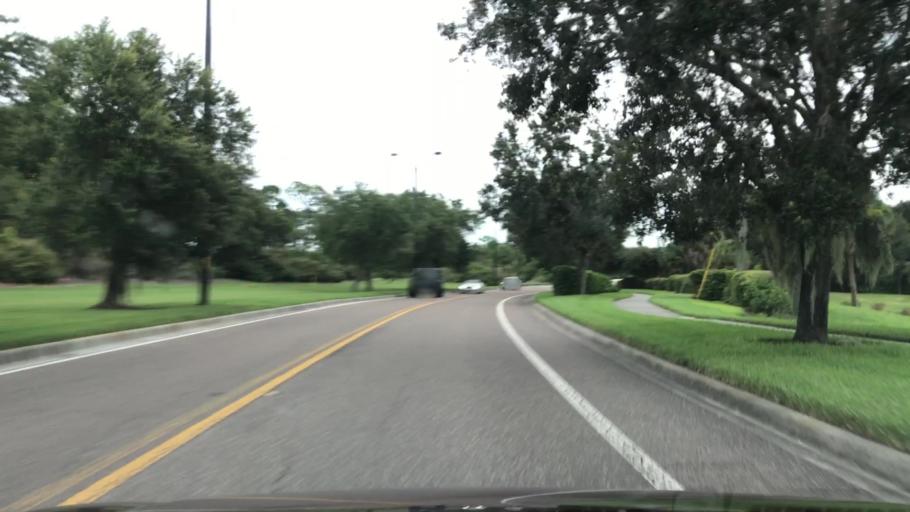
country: US
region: Florida
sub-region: Sarasota County
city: Vamo
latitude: 27.2363
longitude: -82.4822
